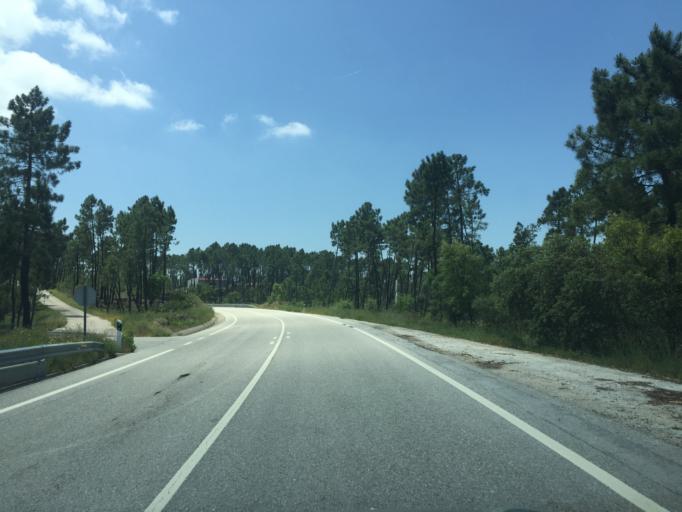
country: PT
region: Castelo Branco
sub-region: Serta
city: Serta
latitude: 39.7618
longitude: -8.1152
